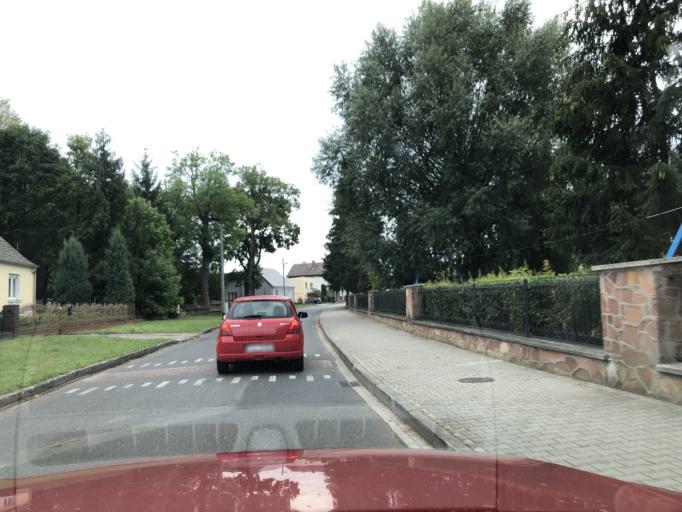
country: PL
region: Greater Poland Voivodeship
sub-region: Powiat szamotulski
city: Pniewy
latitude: 52.5128
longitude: 16.2505
